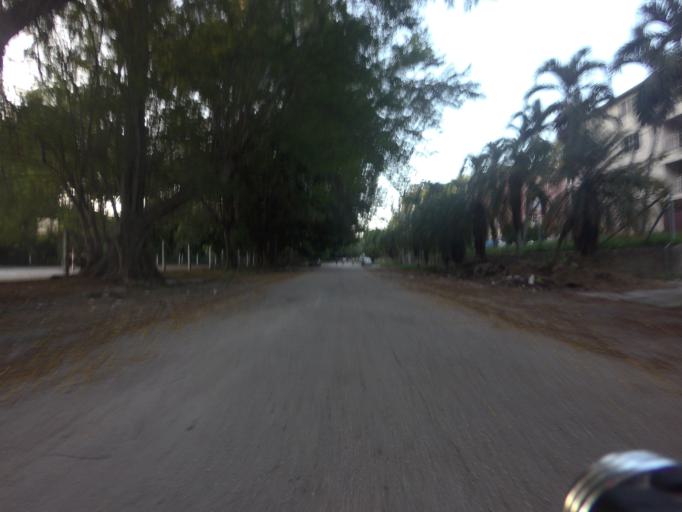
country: CU
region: La Habana
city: Cerro
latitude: 23.1093
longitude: -82.4048
